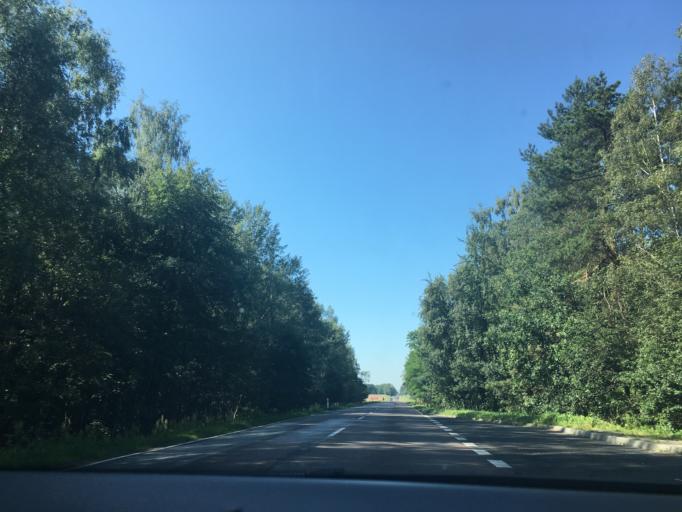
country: PL
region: Lublin Voivodeship
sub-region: Powiat radzynski
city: Borki
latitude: 51.7066
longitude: 22.5163
